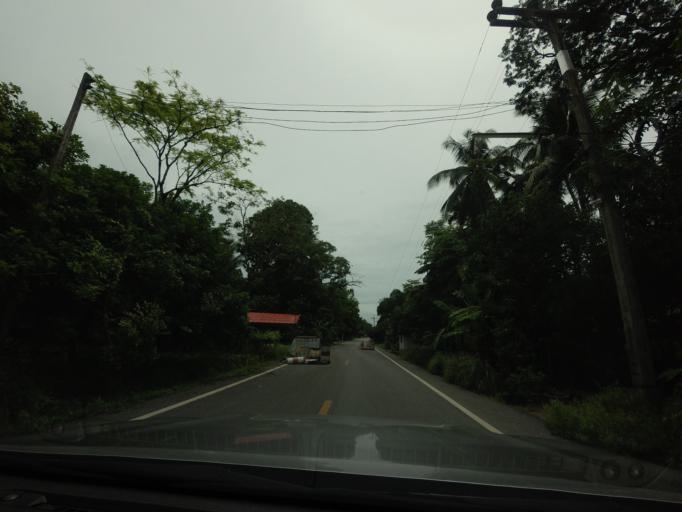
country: TH
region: Pattani
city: Kapho
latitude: 6.6273
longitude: 101.5470
